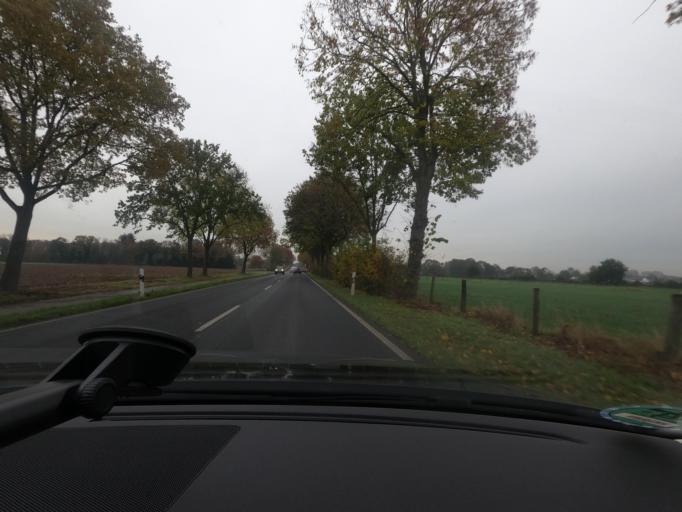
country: DE
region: North Rhine-Westphalia
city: Geldern
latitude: 51.5424
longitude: 6.2872
